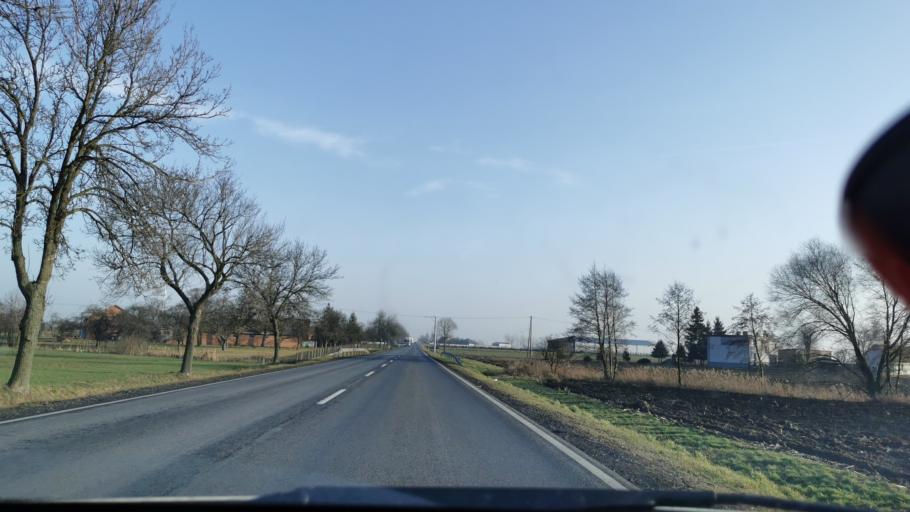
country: PL
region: Lodz Voivodeship
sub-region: Powiat sieradzki
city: Blaszki
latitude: 51.6774
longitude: 18.3525
